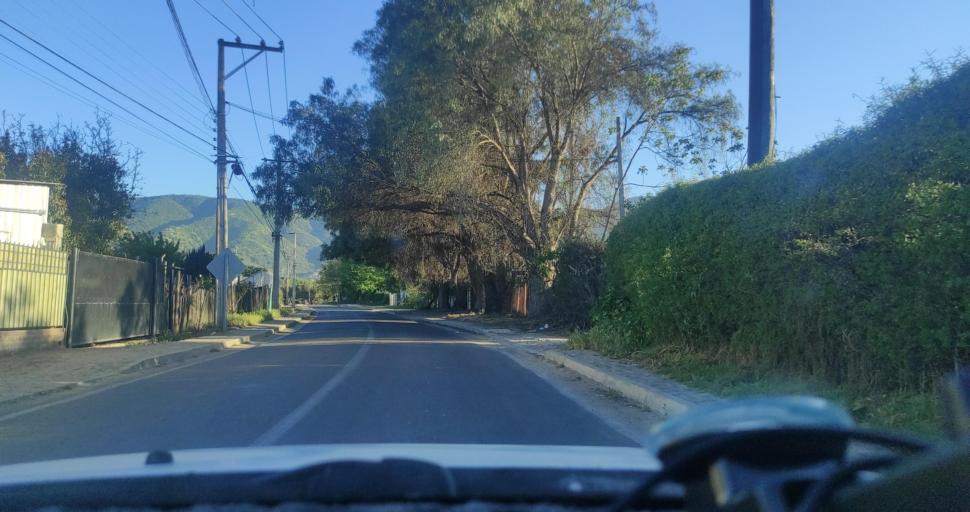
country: CL
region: Valparaiso
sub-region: Provincia de Marga Marga
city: Limache
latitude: -33.0043
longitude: -71.2237
